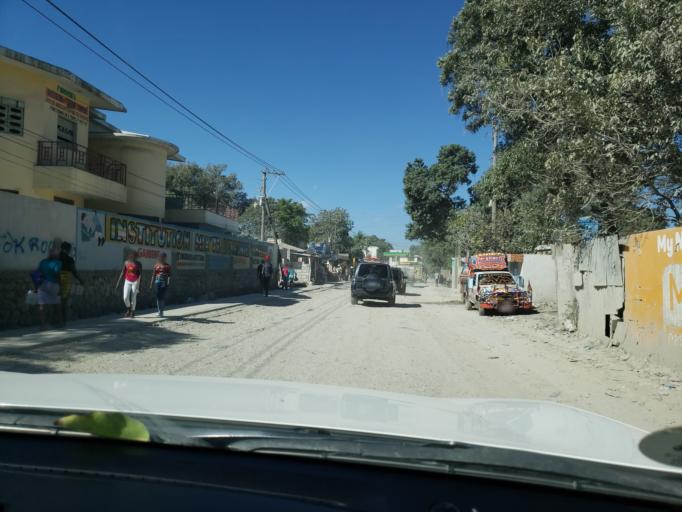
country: HT
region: Ouest
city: Croix des Bouquets
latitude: 18.5734
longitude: -72.2260
